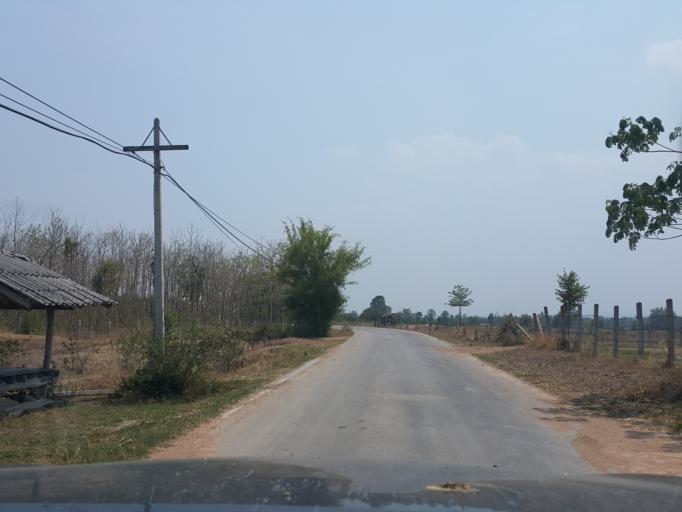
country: TH
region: Lampang
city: Mae Phrik
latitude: 17.5298
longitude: 99.1486
